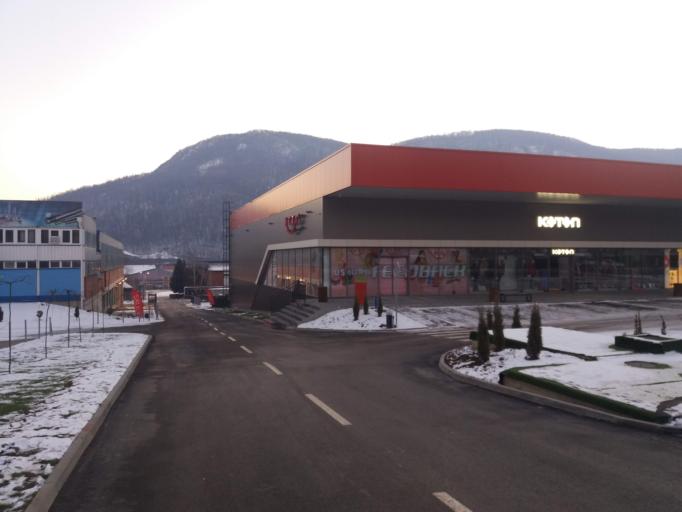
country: RS
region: Central Serbia
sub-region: Zlatiborski Okrug
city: Uzice
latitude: 43.8516
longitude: 19.8567
